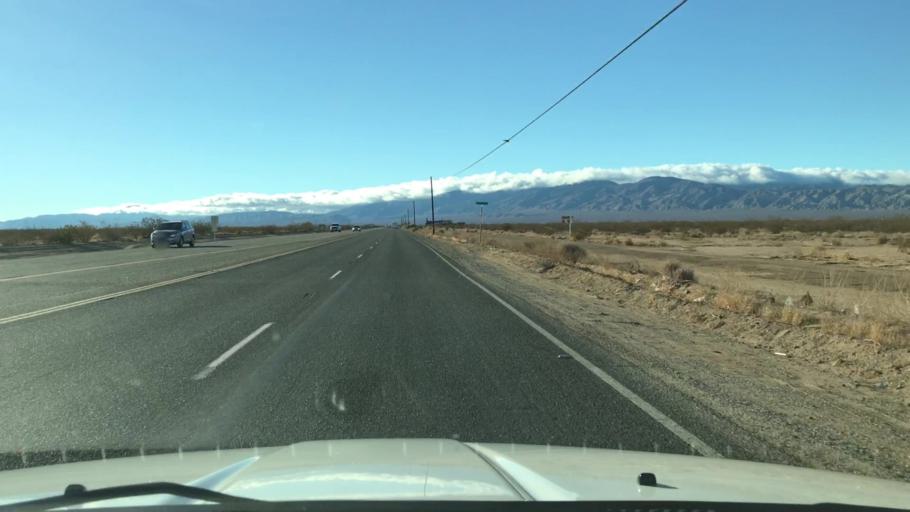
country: US
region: California
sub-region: Kern County
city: California City
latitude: 35.1257
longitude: -118.0148
